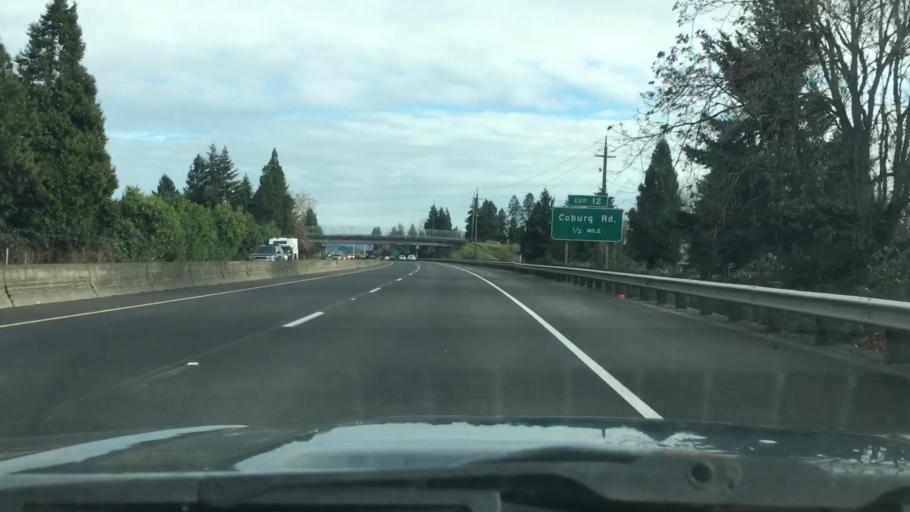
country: US
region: Oregon
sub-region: Lane County
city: Eugene
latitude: 44.0883
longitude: -123.0846
